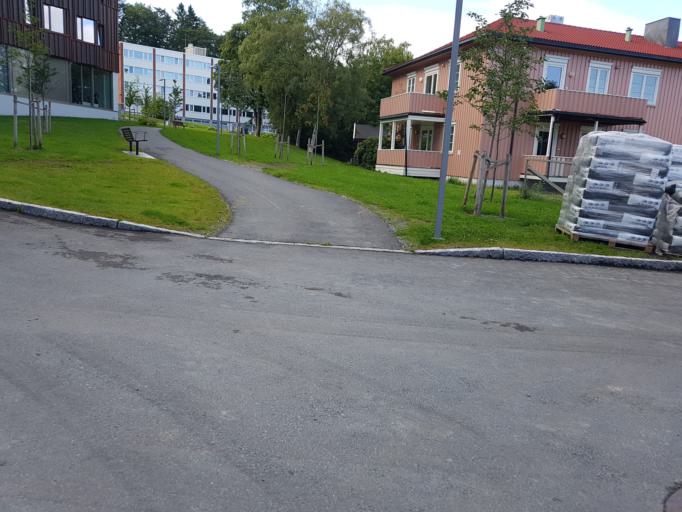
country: NO
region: Sor-Trondelag
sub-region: Trondheim
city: Trondheim
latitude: 63.4291
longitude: 10.4403
